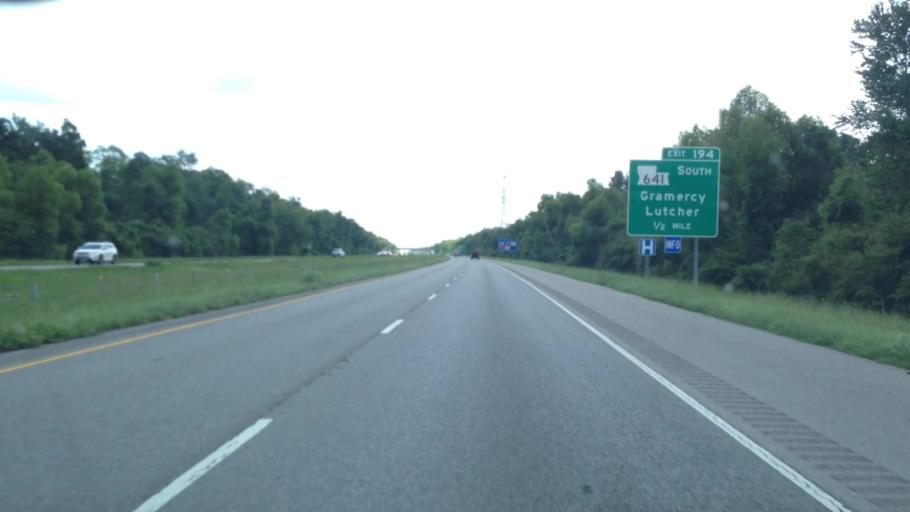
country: US
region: Louisiana
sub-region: Saint James Parish
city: Gramercy
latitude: 30.1247
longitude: -90.6949
